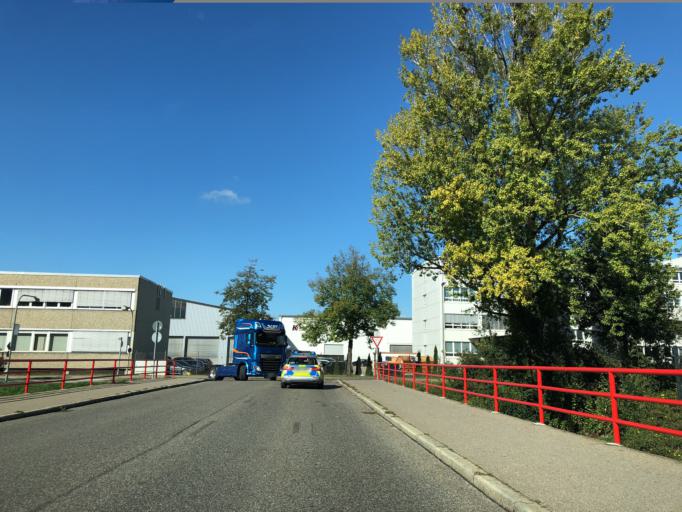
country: DE
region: Baden-Wuerttemberg
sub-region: Tuebingen Region
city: Ulm
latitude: 48.3681
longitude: 9.9541
